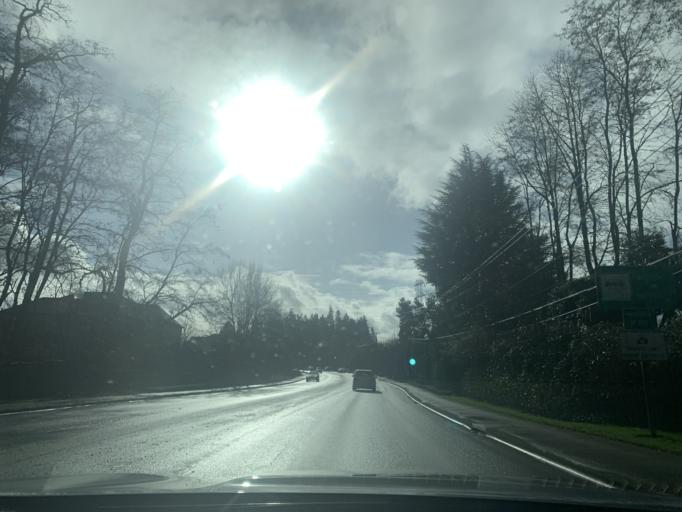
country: US
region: Oregon
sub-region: Washington County
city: Sherwood
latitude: 45.3745
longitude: -122.8568
